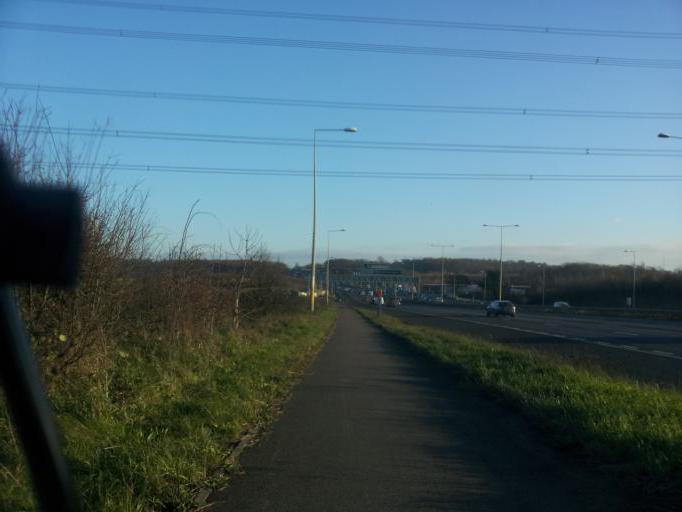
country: GB
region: England
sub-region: Kent
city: Gravesend
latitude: 51.4070
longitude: 0.3915
